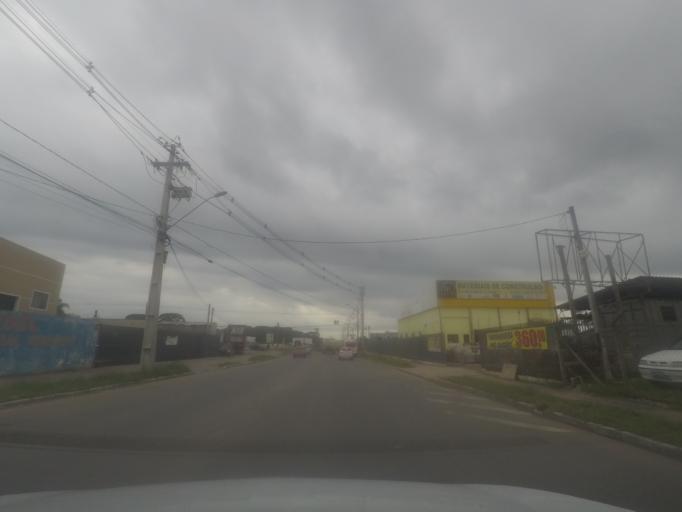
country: BR
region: Parana
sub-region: Sao Jose Dos Pinhais
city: Sao Jose dos Pinhais
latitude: -25.5619
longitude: -49.2668
